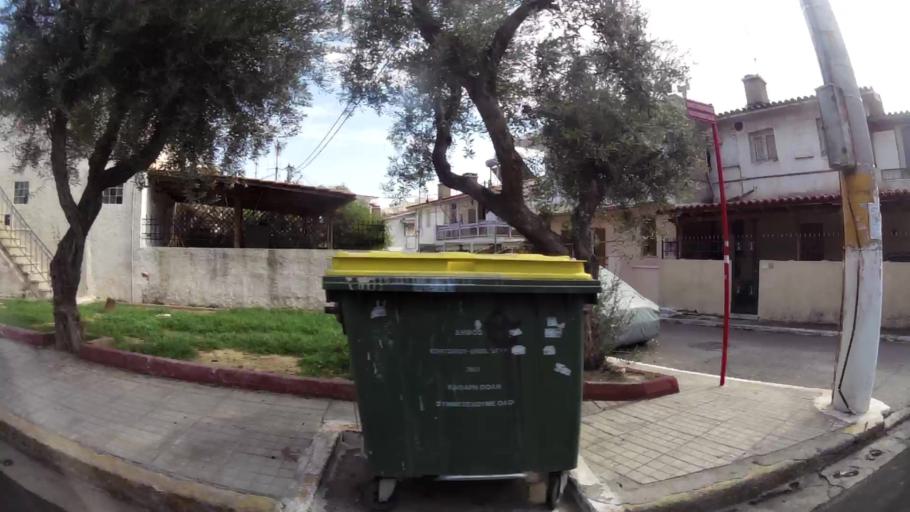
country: GR
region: Attica
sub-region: Nomos Piraios
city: Keratsini
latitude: 37.9609
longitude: 23.6249
